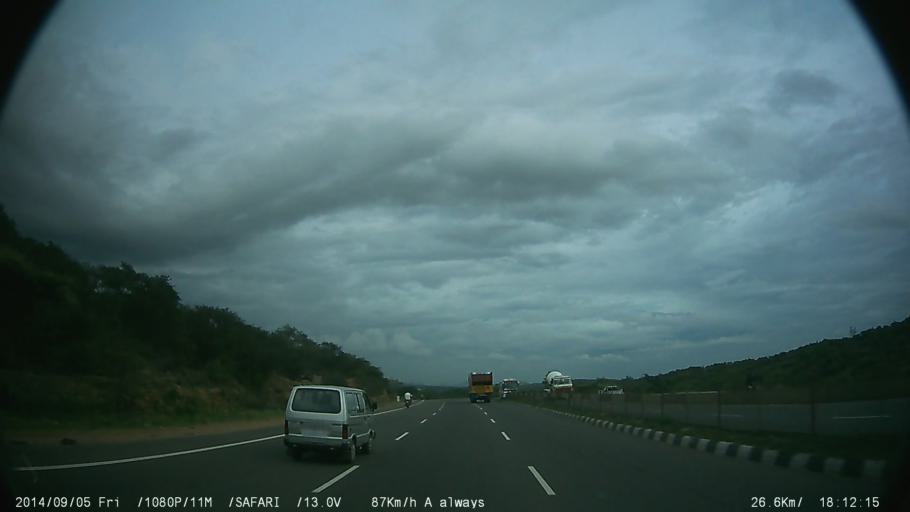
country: IN
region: Tamil Nadu
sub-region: Krishnagiri
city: Hosur
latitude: 12.6945
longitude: 77.9162
